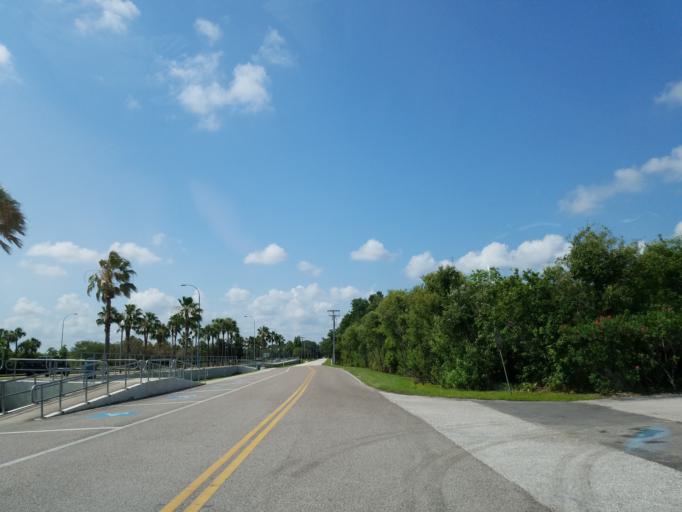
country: US
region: Florida
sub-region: Hillsborough County
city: Brandon
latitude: 27.9243
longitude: -82.3021
